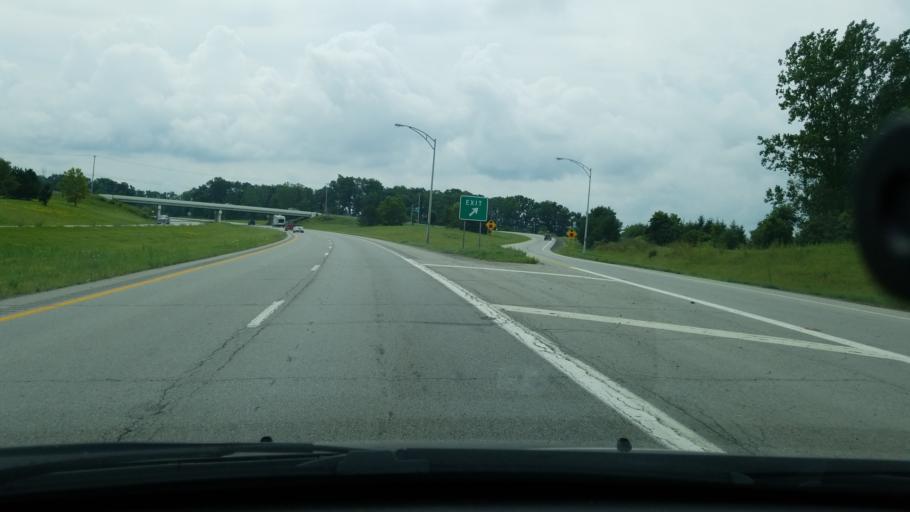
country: US
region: Ohio
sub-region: Erie County
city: Huron
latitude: 41.3730
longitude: -82.5716
